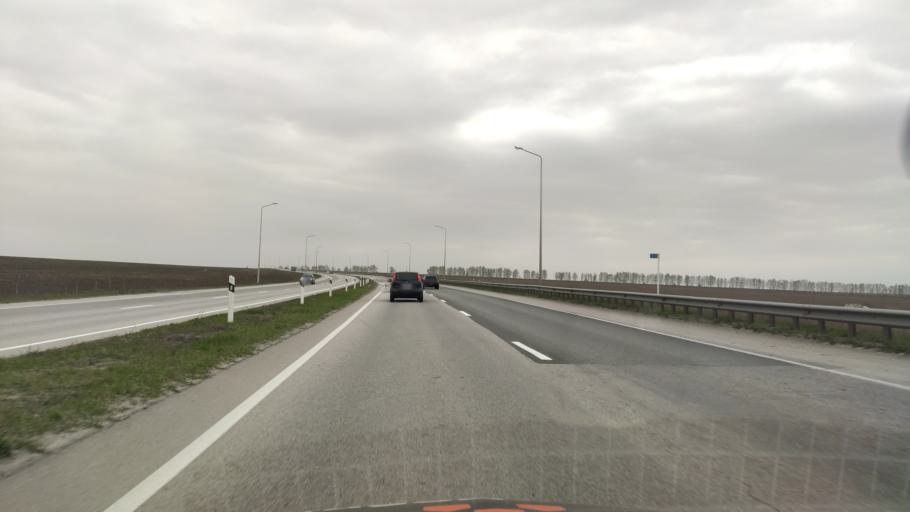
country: RU
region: Belgorod
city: Staryy Oskol
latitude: 51.3379
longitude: 37.7709
